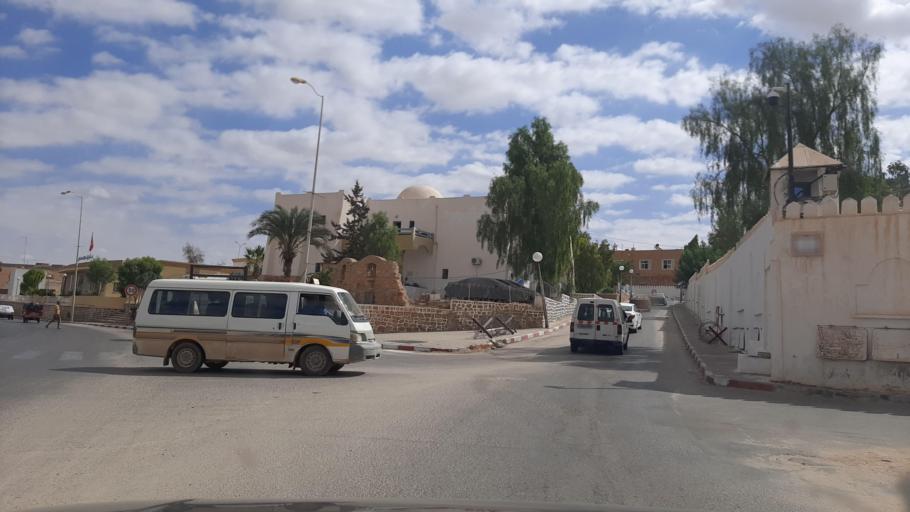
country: TN
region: Tataouine
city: Tataouine
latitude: 32.9267
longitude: 10.4432
